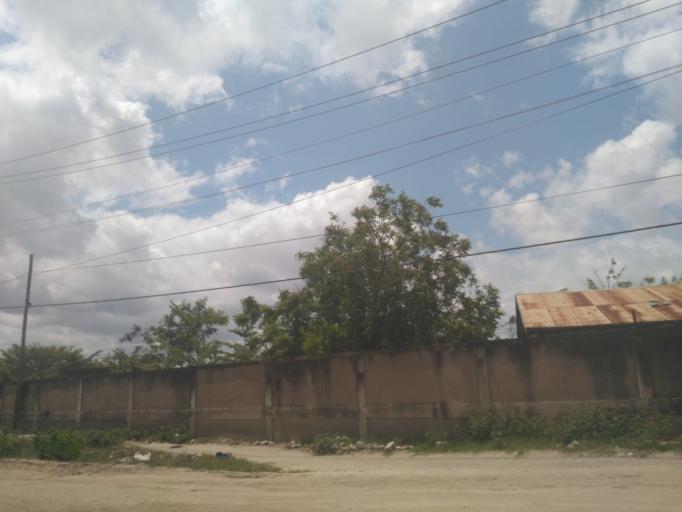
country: TZ
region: Dar es Salaam
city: Dar es Salaam
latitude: -6.8391
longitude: 39.2881
